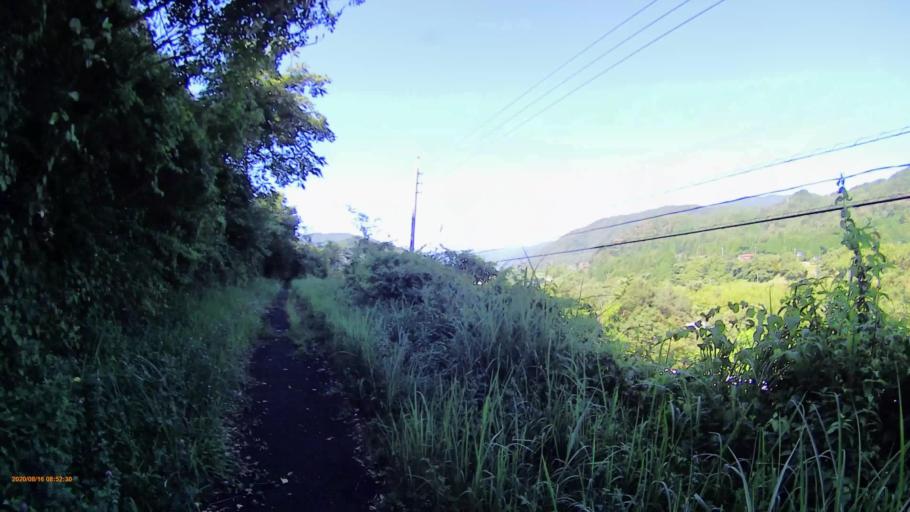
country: JP
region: Nagano
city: Iida
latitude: 35.7029
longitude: 137.6989
